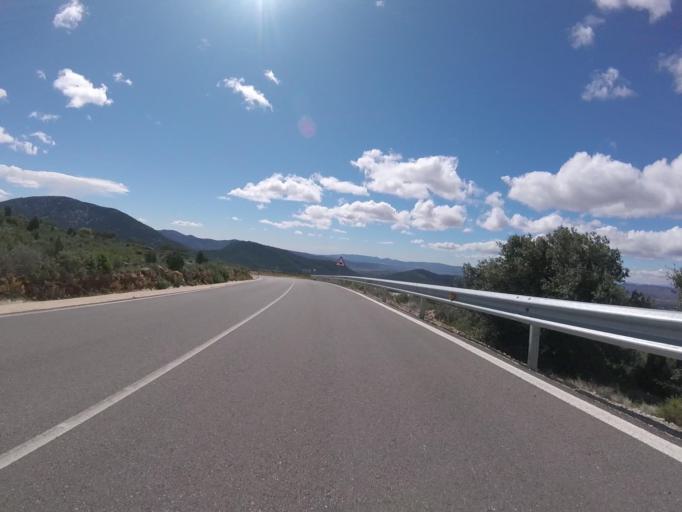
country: ES
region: Valencia
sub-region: Provincia de Castello
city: Culla
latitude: 40.3005
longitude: -0.1268
